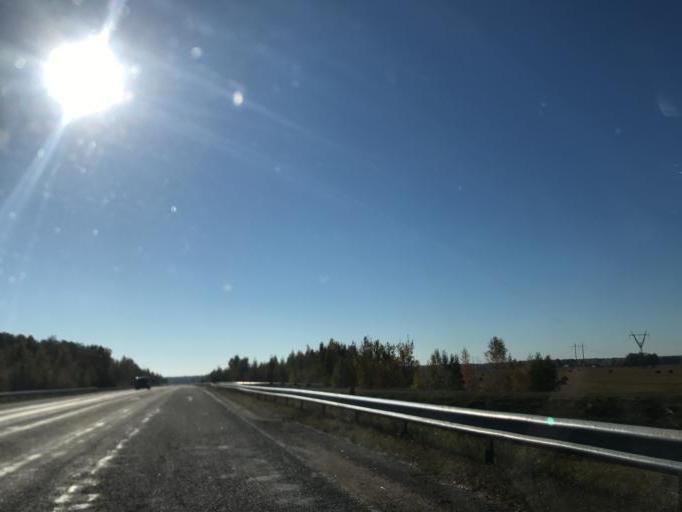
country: BY
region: Mogilev
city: Babruysk
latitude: 53.1044
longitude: 29.0566
